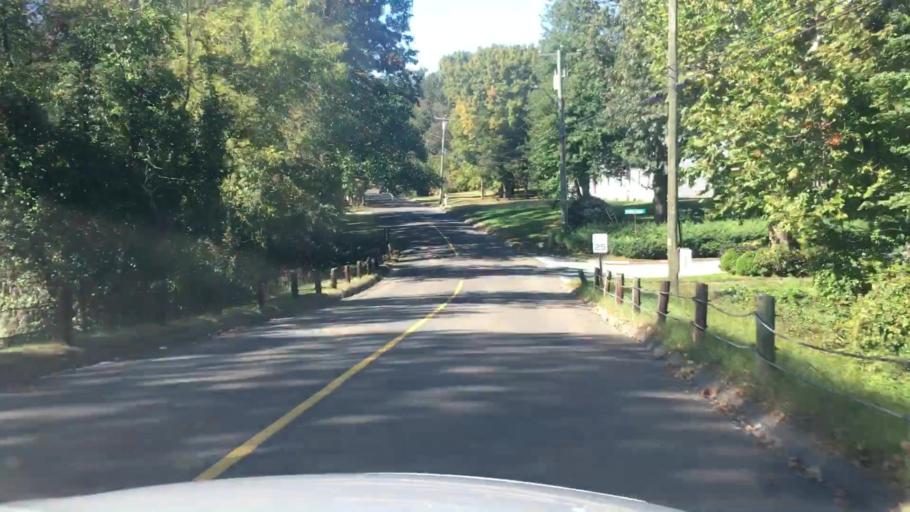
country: US
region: Connecticut
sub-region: Middlesex County
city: Westbrook Center
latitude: 41.3012
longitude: -72.4436
